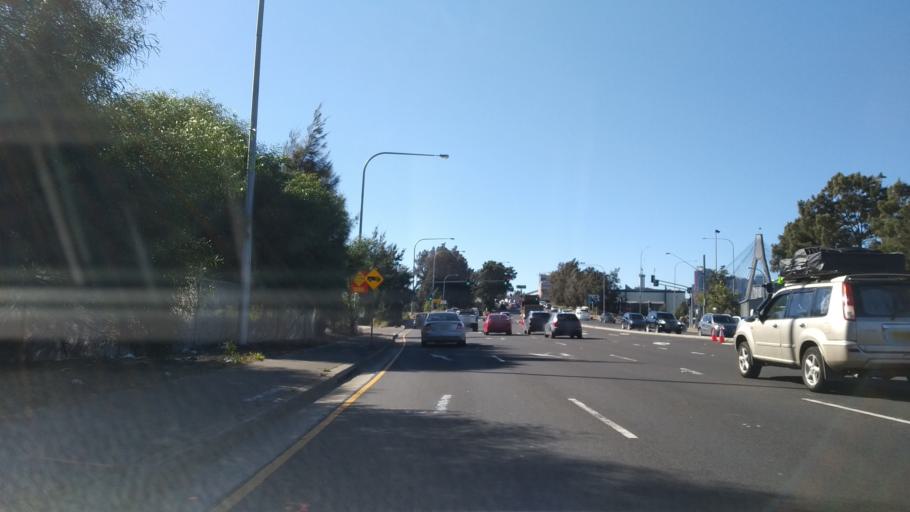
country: AU
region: New South Wales
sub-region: Leichhardt
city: Lilyfield
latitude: -33.8705
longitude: 151.1736
